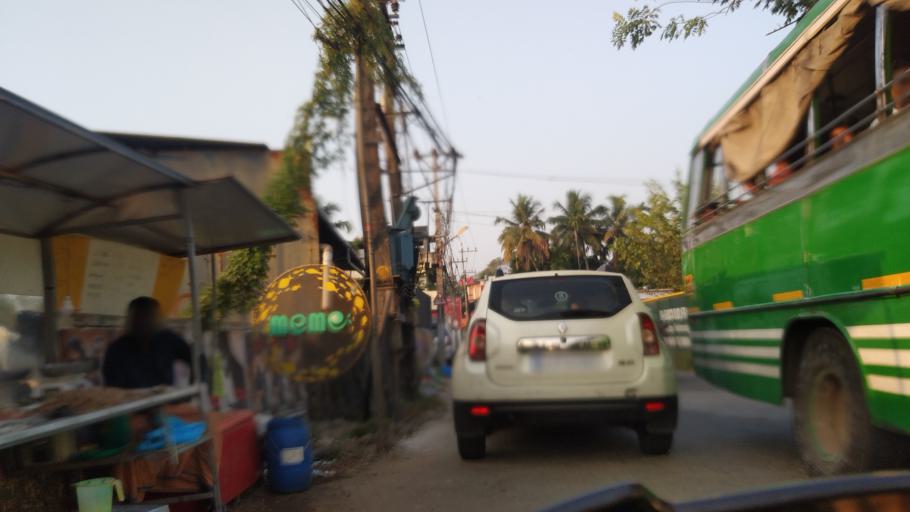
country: IN
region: Kerala
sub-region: Ernakulam
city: Elur
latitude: 10.0290
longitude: 76.2753
